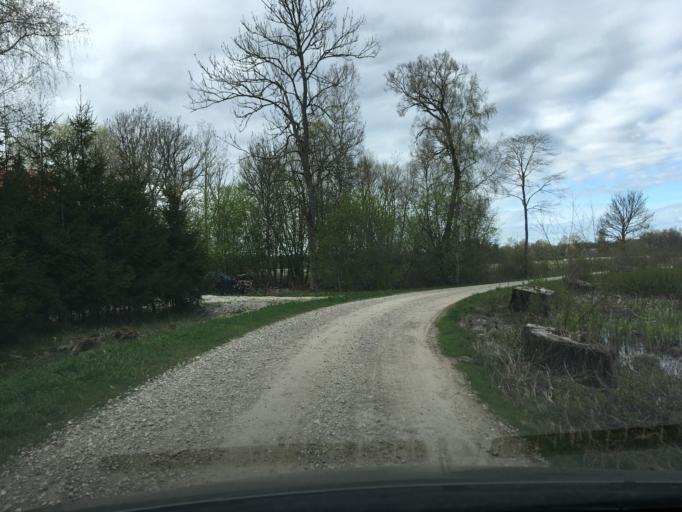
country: EE
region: Laeaene
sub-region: Lihula vald
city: Lihula
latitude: 58.5765
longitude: 23.7233
